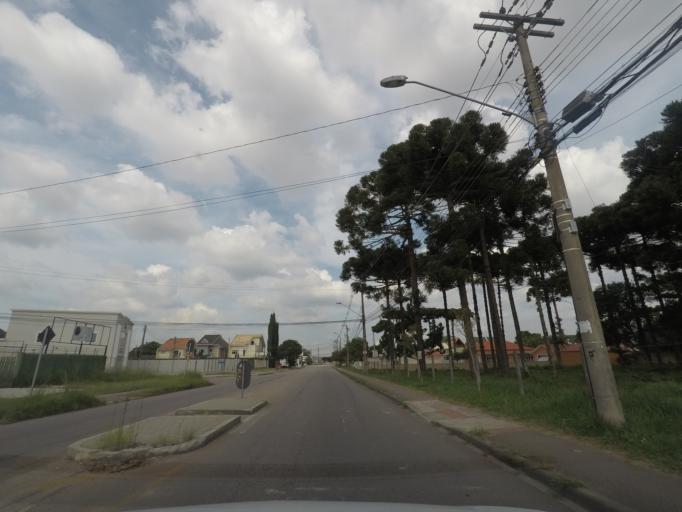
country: BR
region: Parana
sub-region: Sao Jose Dos Pinhais
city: Sao Jose dos Pinhais
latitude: -25.4978
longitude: -49.2151
